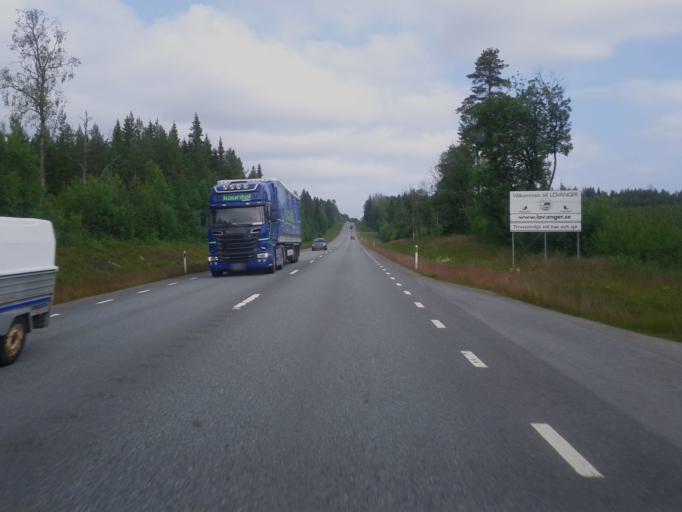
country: SE
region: Vaesterbotten
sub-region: Skelleftea Kommun
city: Burea
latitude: 64.3535
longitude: 21.2942
